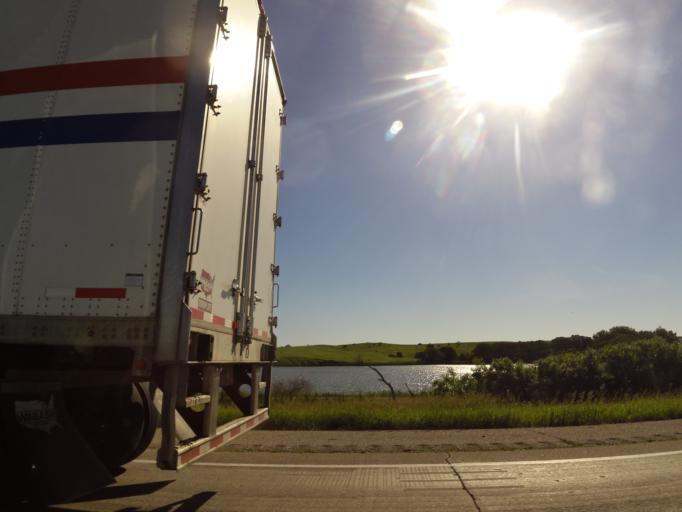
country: US
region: Minnesota
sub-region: Grant County
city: Elbow Lake
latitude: 46.0505
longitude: -95.8487
